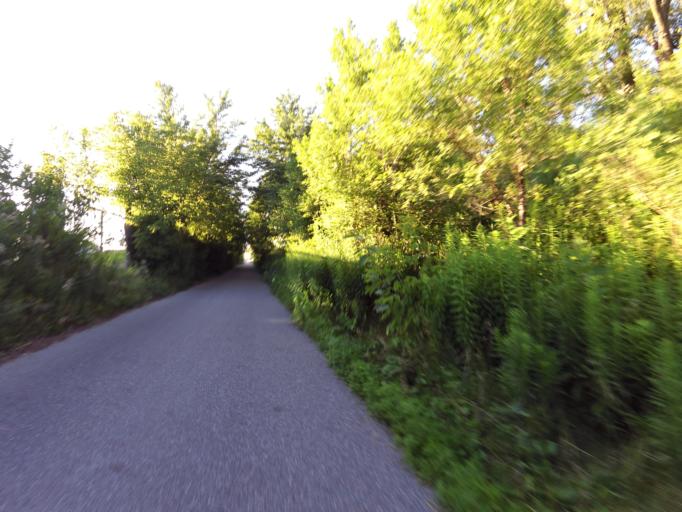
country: CA
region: Ontario
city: Toronto
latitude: 43.6654
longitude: -79.4579
